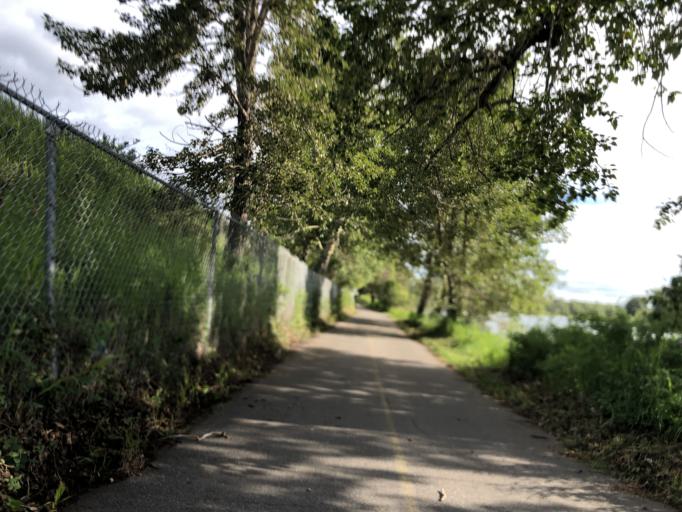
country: CA
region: Alberta
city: Calgary
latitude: 51.0183
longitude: -114.0129
